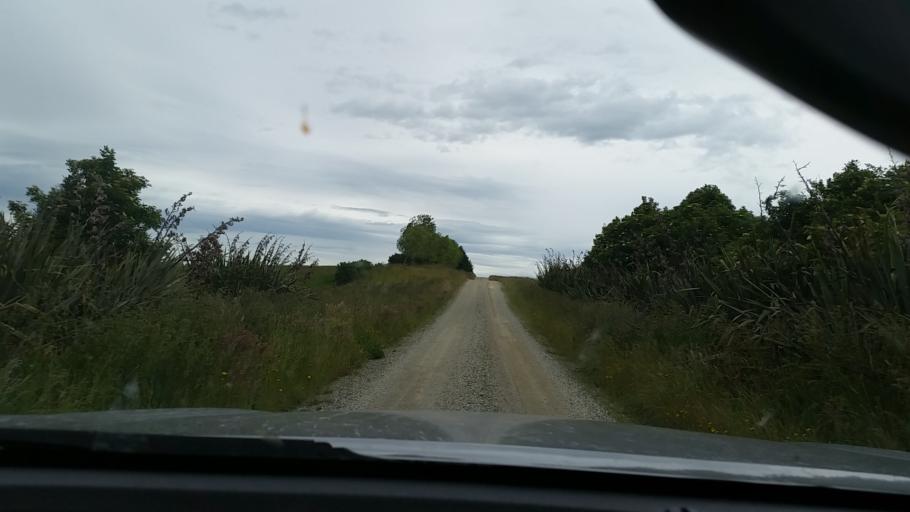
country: NZ
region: Southland
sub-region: Invercargill City
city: Invercargill
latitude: -46.2705
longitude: 168.5333
